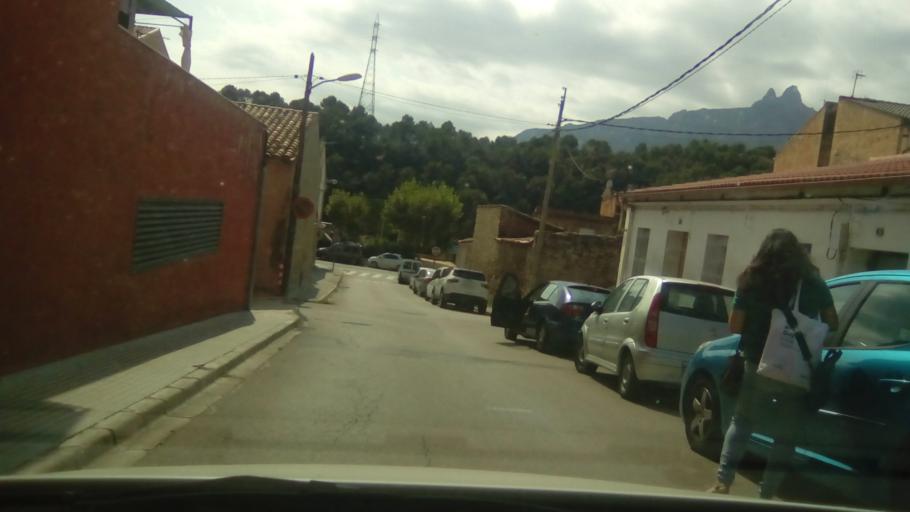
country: ES
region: Catalonia
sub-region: Provincia de Barcelona
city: Monistrol de Montserrat
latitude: 41.6293
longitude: 1.8623
